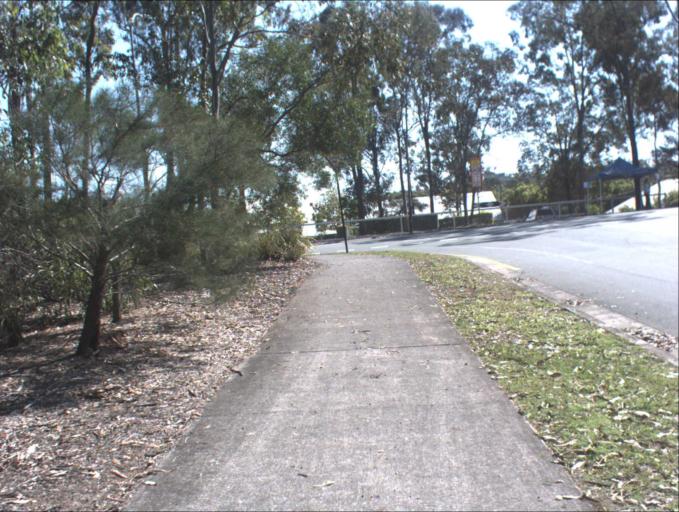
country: AU
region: Queensland
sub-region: Logan
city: Waterford West
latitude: -27.7107
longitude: 153.1514
